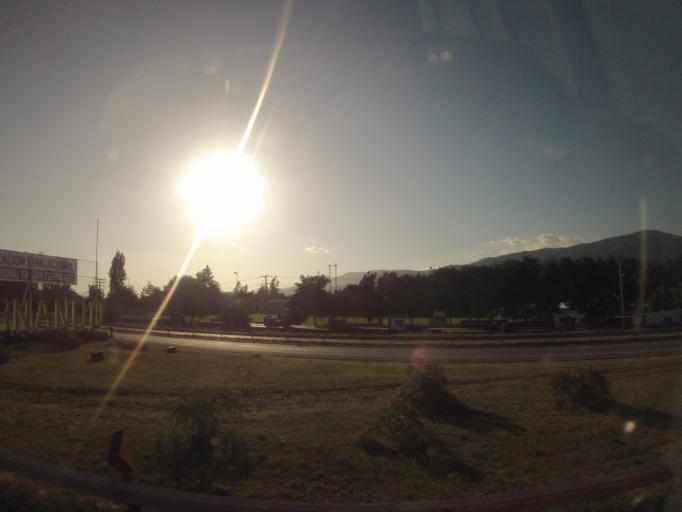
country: CL
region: O'Higgins
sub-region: Provincia de Colchagua
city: Chimbarongo
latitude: -34.5714
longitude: -70.9721
